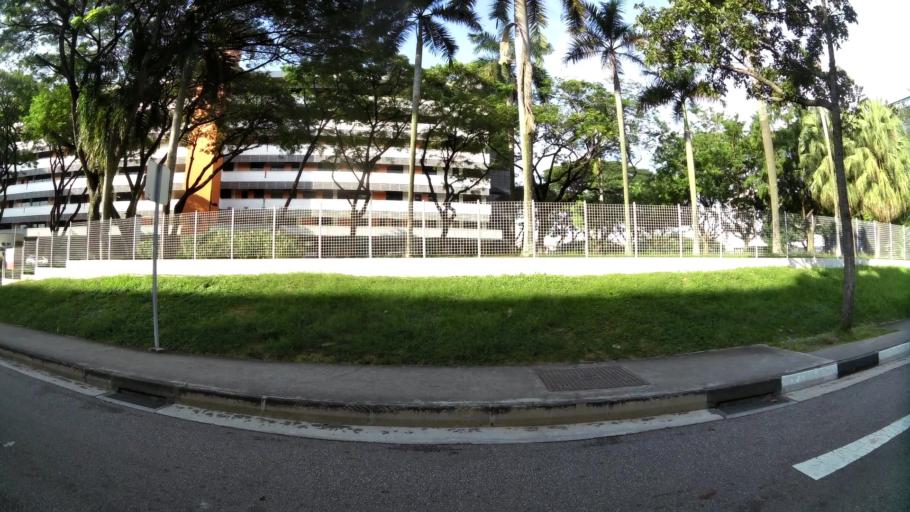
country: SG
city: Singapore
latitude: 1.3229
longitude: 103.8751
